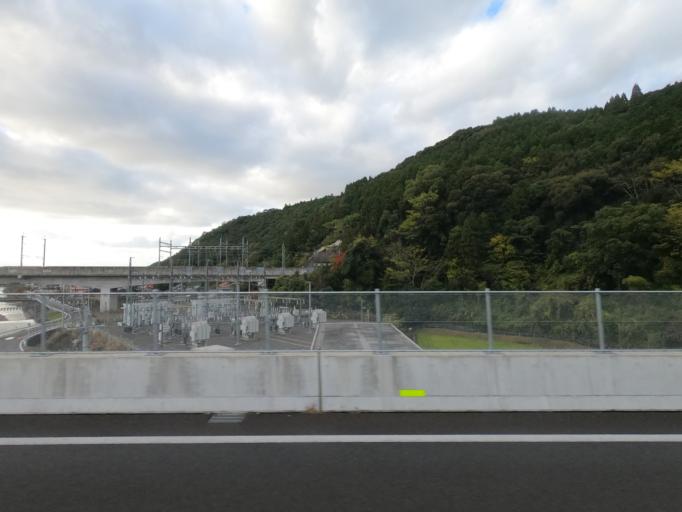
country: JP
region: Kumamoto
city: Minamata
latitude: 32.2342
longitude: 130.4548
